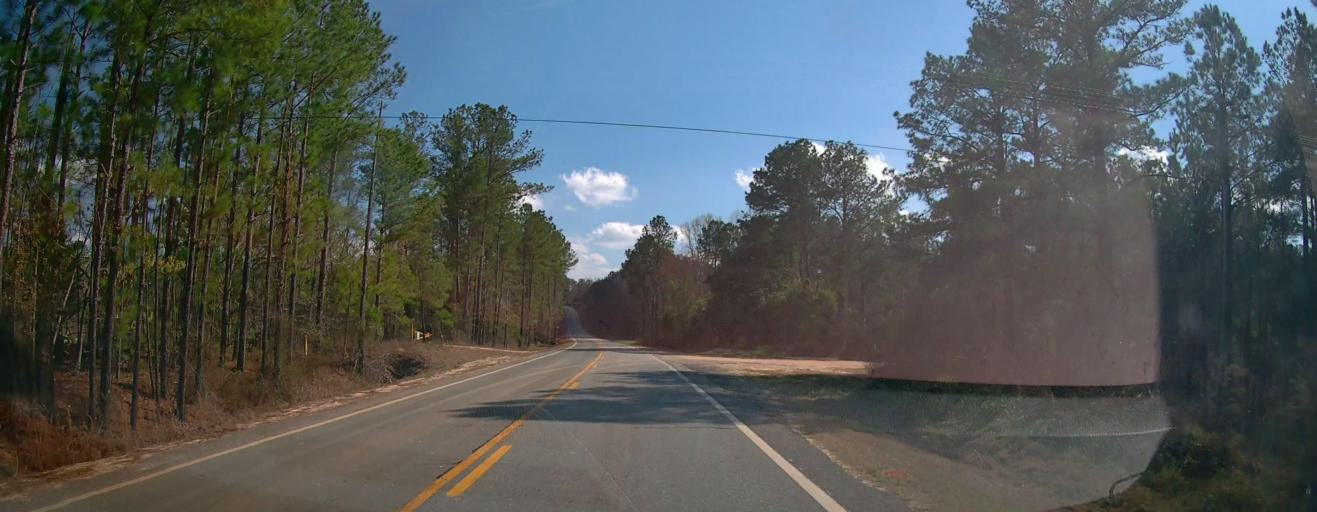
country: US
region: Georgia
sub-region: Wilkinson County
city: Gordon
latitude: 32.8298
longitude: -83.3292
